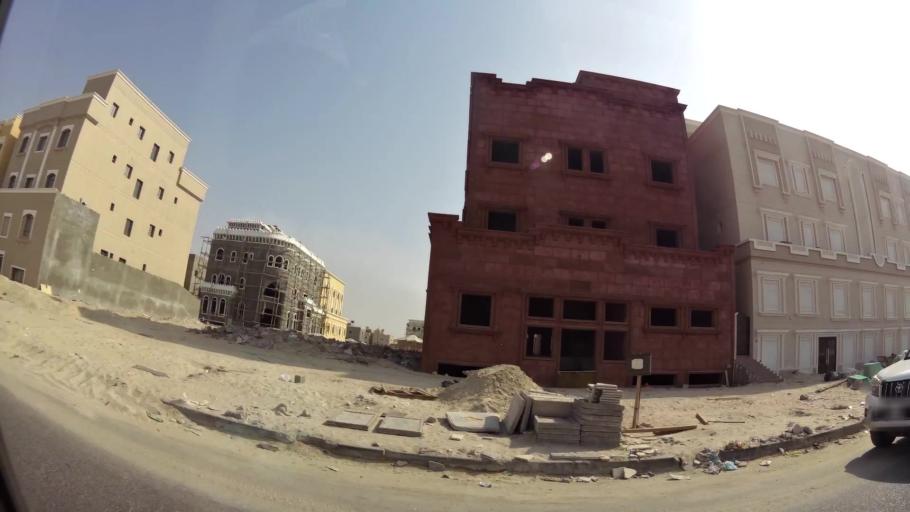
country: KW
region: Muhafazat al Jahra'
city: Al Jahra'
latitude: 29.3524
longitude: 47.7709
